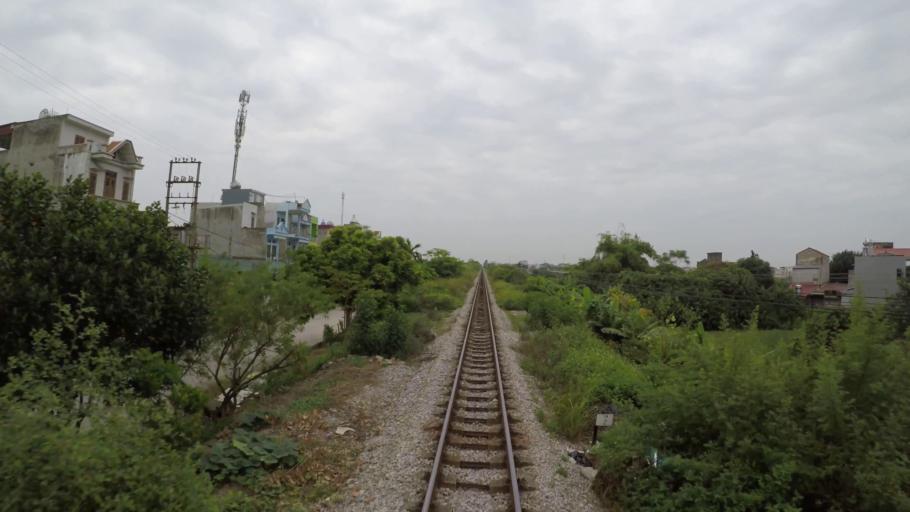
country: VN
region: Hai Duong
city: Thanh Pho Hai Duong
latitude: 20.9435
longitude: 106.3591
